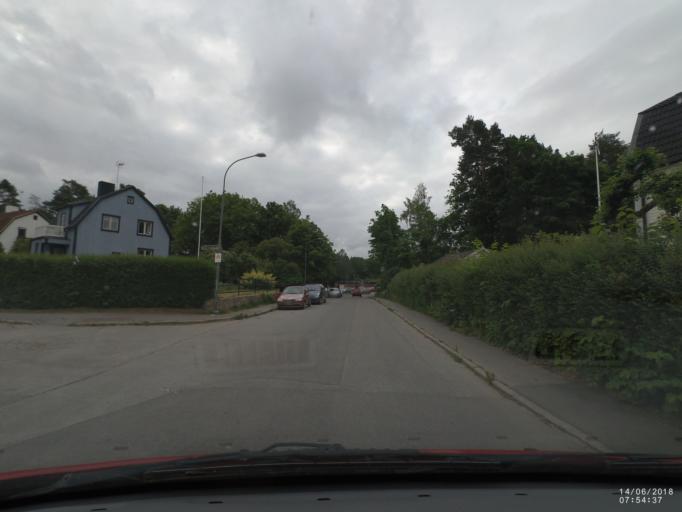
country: SE
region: Soedermanland
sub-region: Nykopings Kommun
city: Nykoping
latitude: 58.7600
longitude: 17.0250
